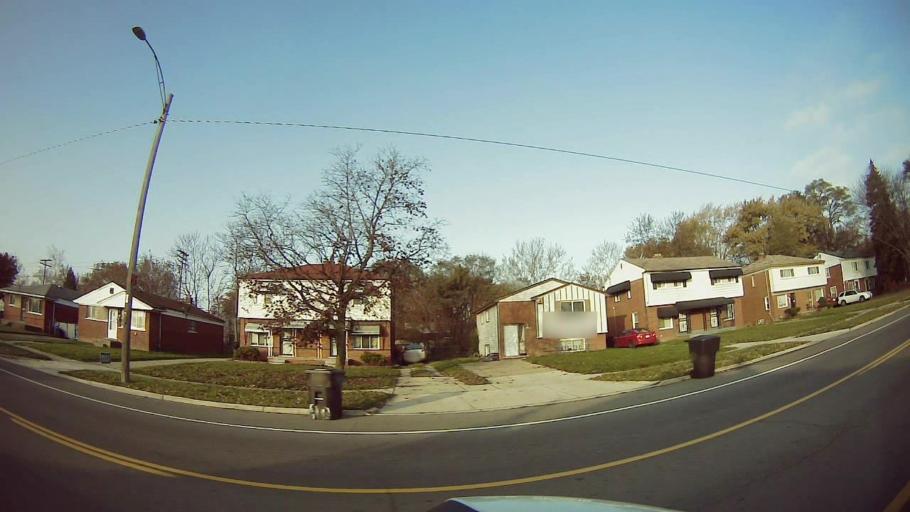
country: US
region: Michigan
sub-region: Wayne County
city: Dearborn
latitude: 42.3575
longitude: -83.1576
